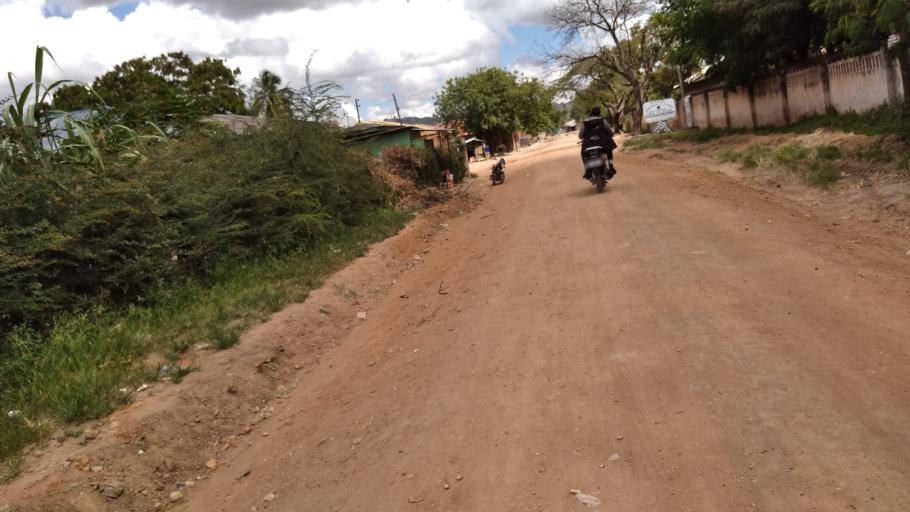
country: TZ
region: Dodoma
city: Dodoma
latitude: -6.1634
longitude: 35.7385
